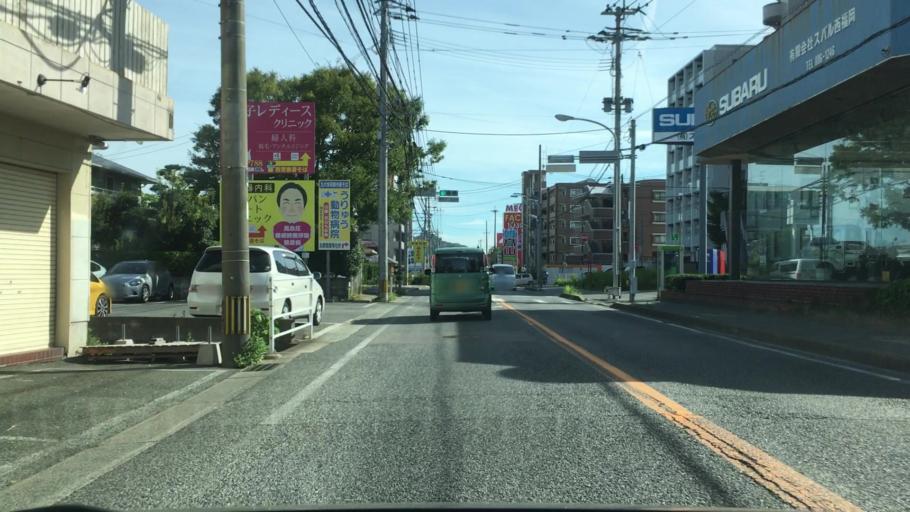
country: JP
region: Fukuoka
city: Maebaru-chuo
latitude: 33.5764
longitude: 130.2517
